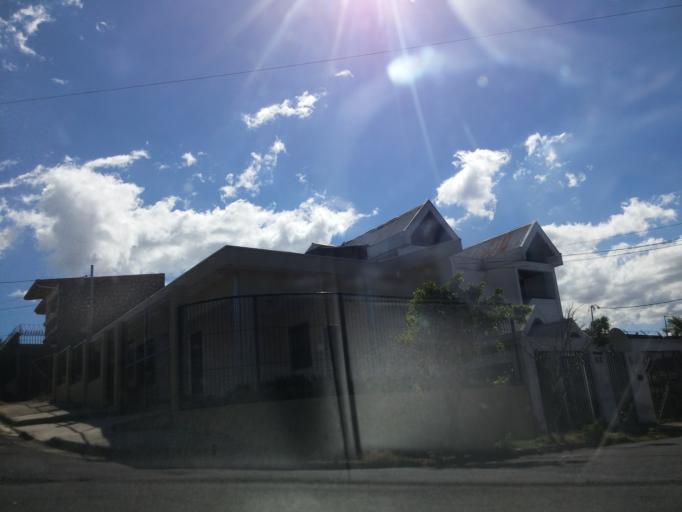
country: CR
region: San Jose
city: Colima
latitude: 9.9432
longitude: -84.0925
